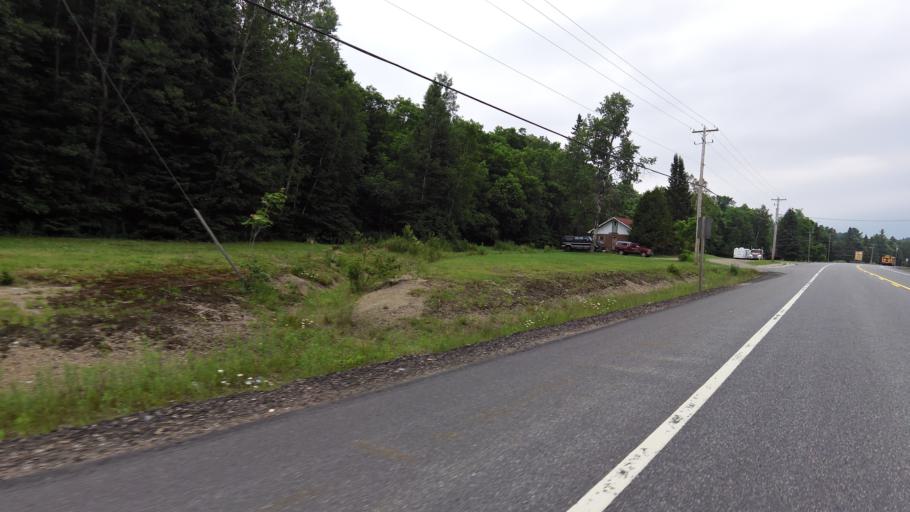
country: CA
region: Ontario
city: Huntsville
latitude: 45.3821
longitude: -78.9137
